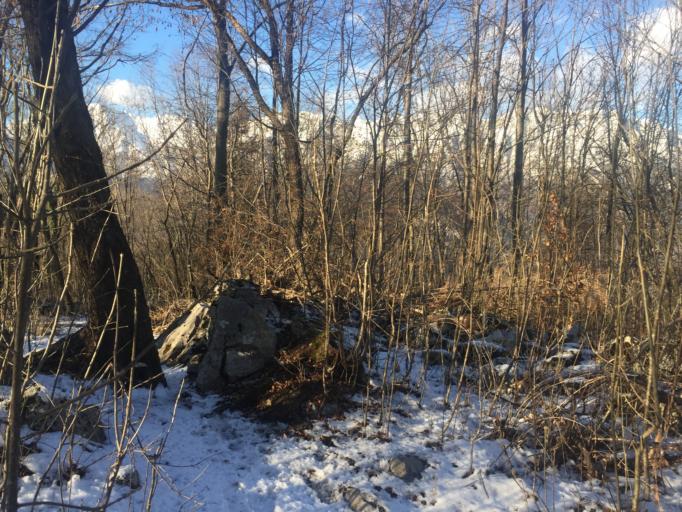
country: IT
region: Friuli Venezia Giulia
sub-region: Provincia di Udine
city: Tarcento
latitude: 46.2487
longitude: 13.2359
